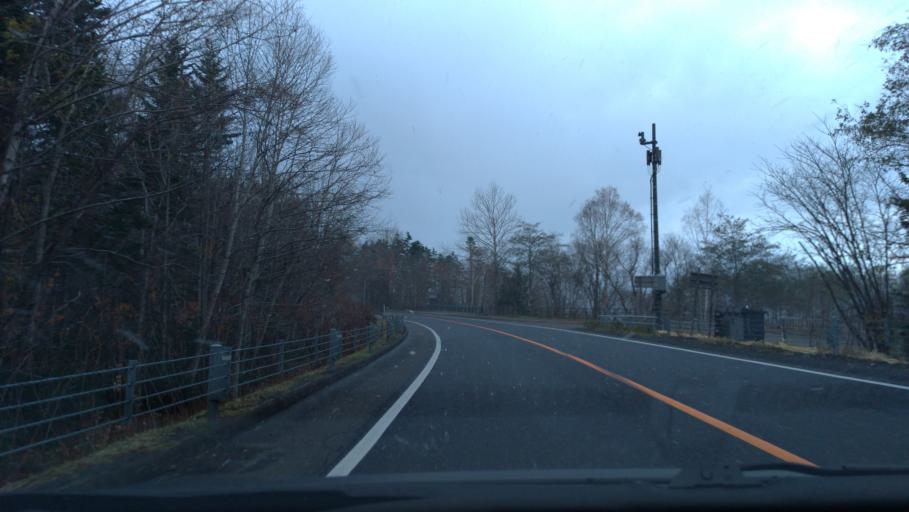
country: JP
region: Hokkaido
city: Shiraoi
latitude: 42.7421
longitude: 141.4031
